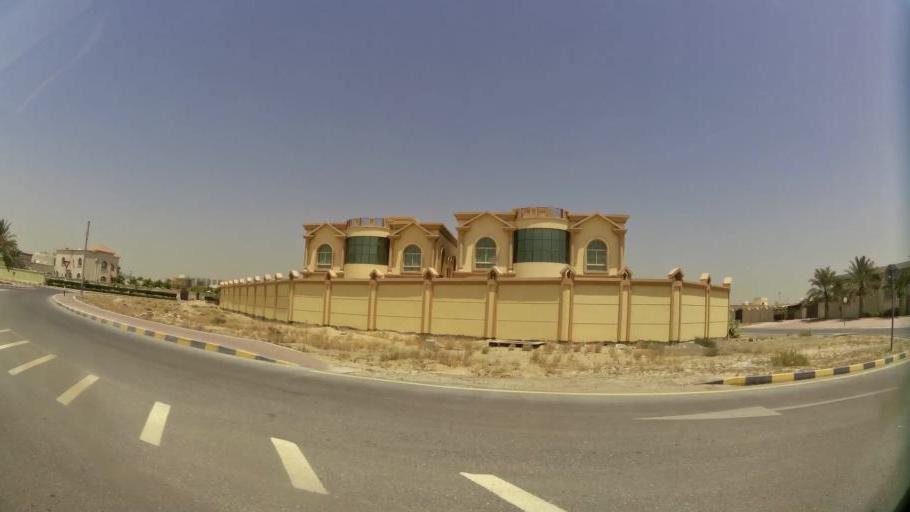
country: AE
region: Ajman
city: Ajman
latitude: 25.4051
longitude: 55.5201
